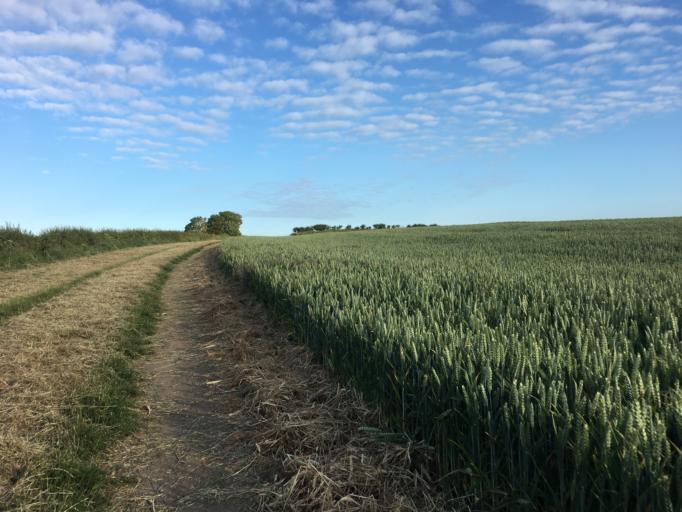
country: GB
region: England
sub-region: Northumberland
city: Bamburgh
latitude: 55.6011
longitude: -1.6988
